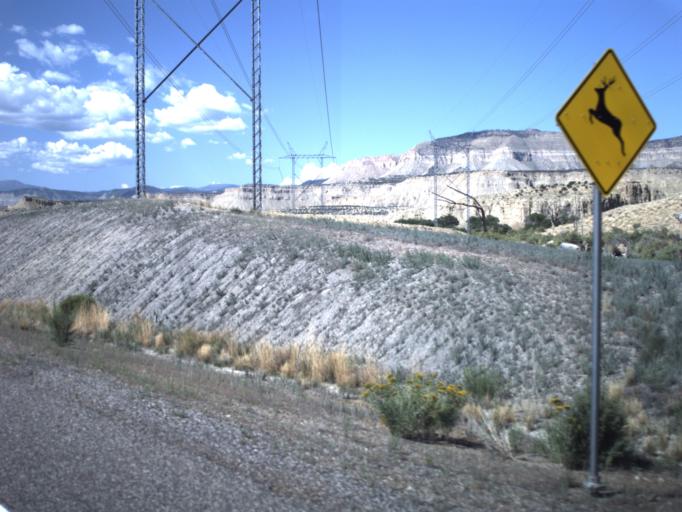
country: US
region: Utah
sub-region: Emery County
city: Ferron
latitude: 38.8829
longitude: -111.2866
